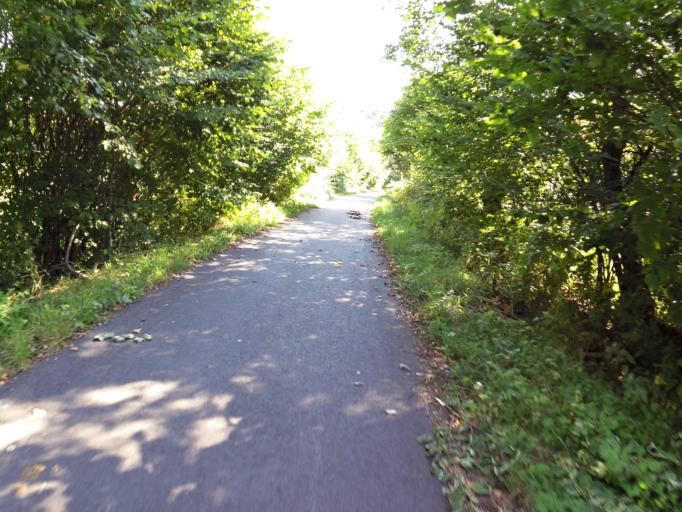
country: BE
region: Wallonia
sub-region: Province de Liege
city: Butgenbach
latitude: 50.4074
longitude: 6.1606
